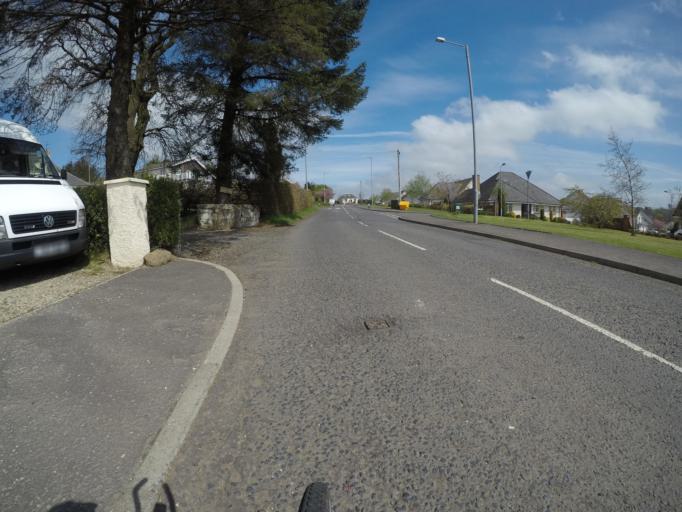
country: GB
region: Scotland
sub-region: East Ayrshire
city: Stewarton
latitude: 55.6870
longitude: -4.5019
